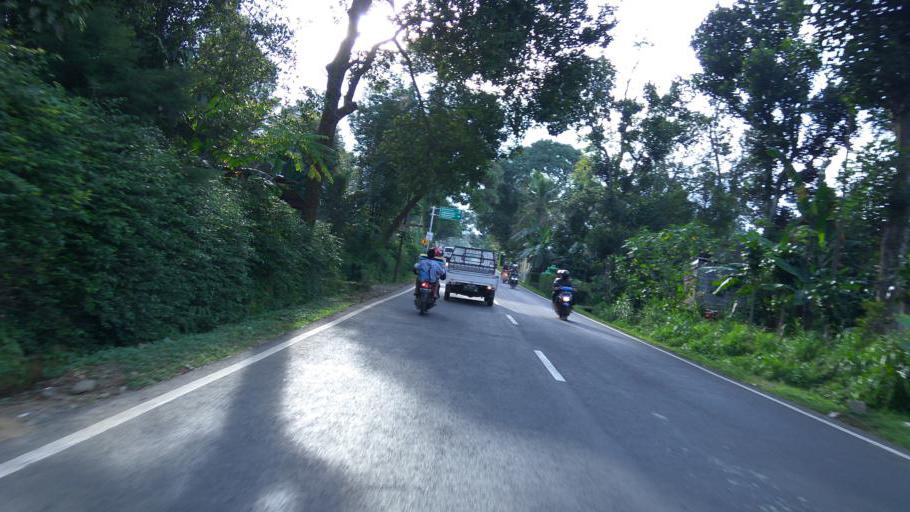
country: ID
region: Central Java
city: Salatiga
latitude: -7.3673
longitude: 110.4614
